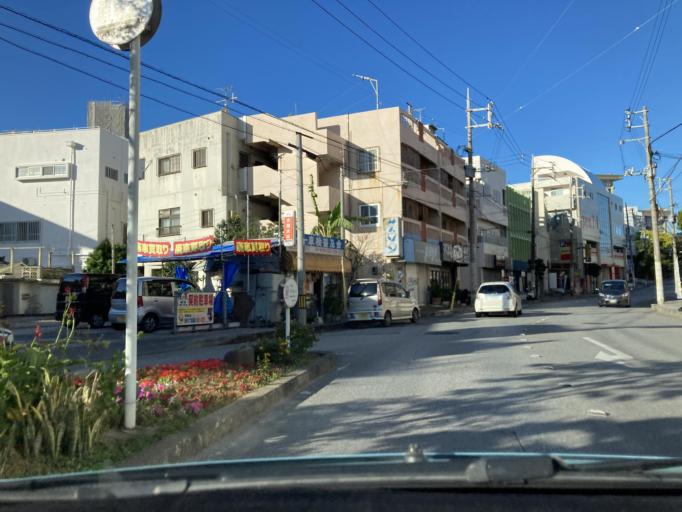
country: JP
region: Okinawa
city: Naha-shi
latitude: 26.2101
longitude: 127.6998
